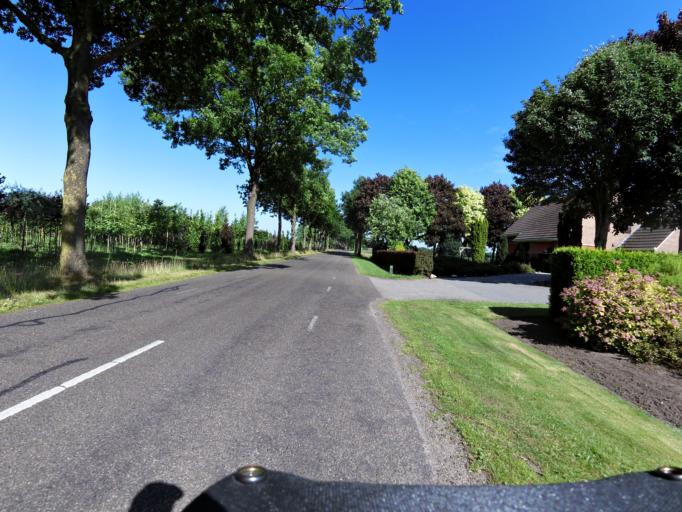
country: NL
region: Overijssel
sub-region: Gemeente Dalfsen
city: Dalfsen
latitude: 52.4735
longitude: 6.3694
